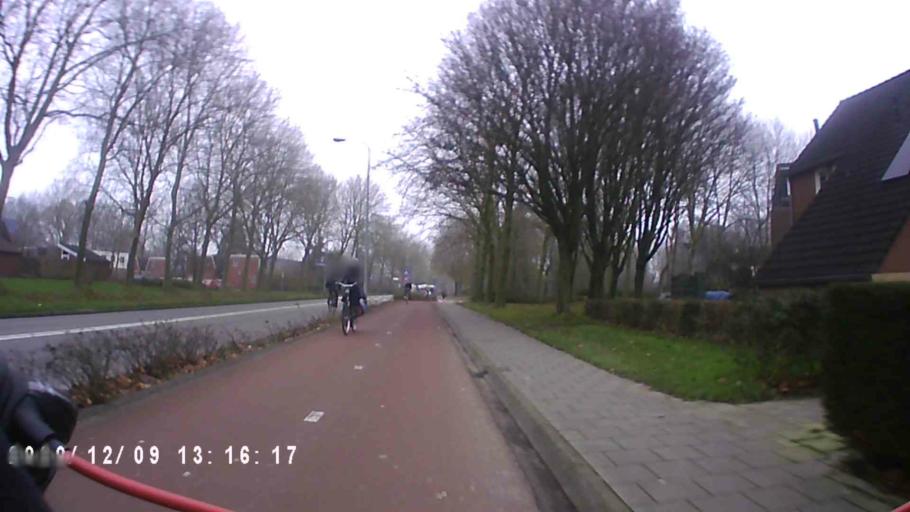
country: NL
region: Groningen
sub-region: Gemeente Groningen
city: Oosterpark
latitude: 53.2483
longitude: 6.5875
